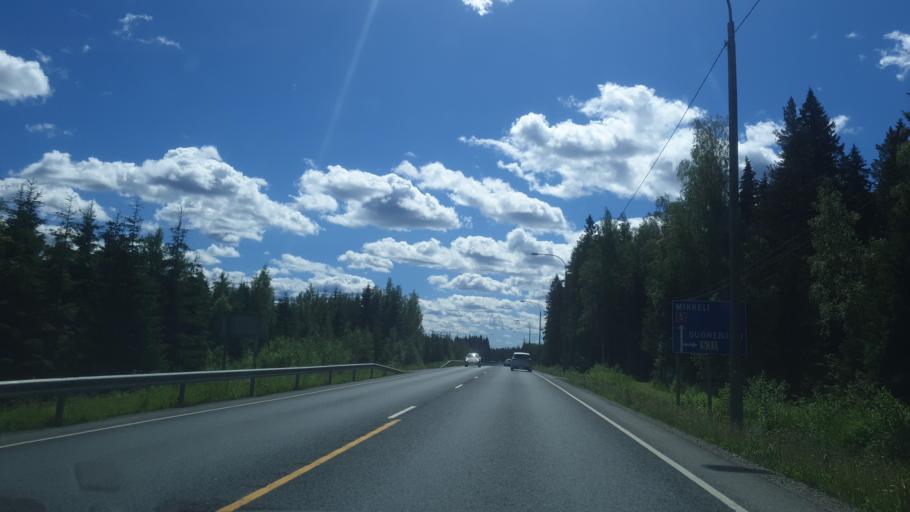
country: FI
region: Northern Savo
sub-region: Varkaus
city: Leppaevirta
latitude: 62.5545
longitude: 27.6200
